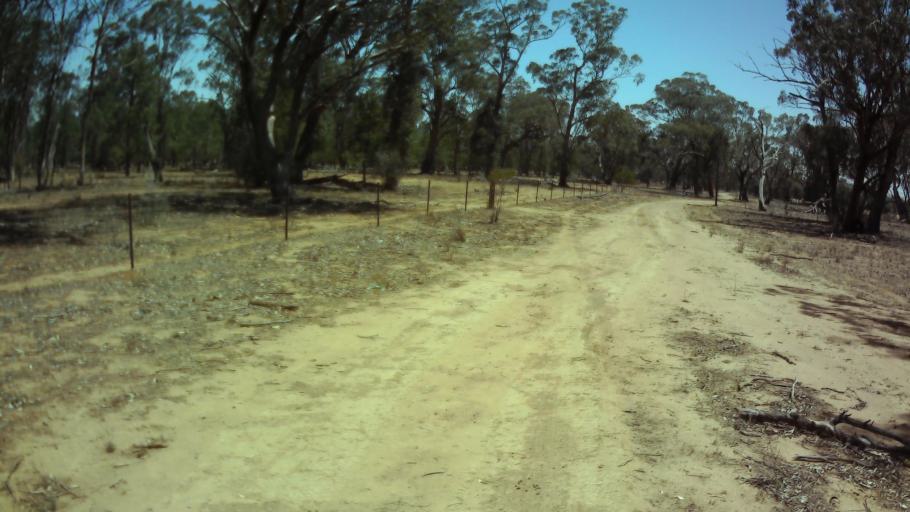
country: AU
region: New South Wales
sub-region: Weddin
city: Grenfell
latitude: -34.0676
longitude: 147.7972
